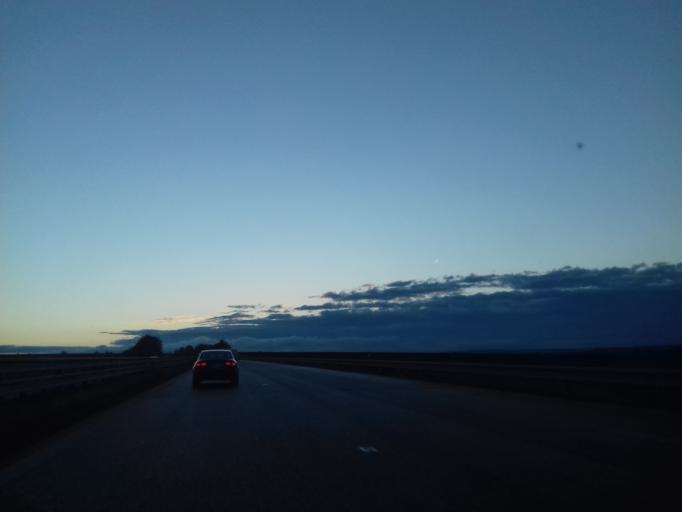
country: CZ
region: South Moravian
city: Tvarozna
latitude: 49.1823
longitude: 16.7715
